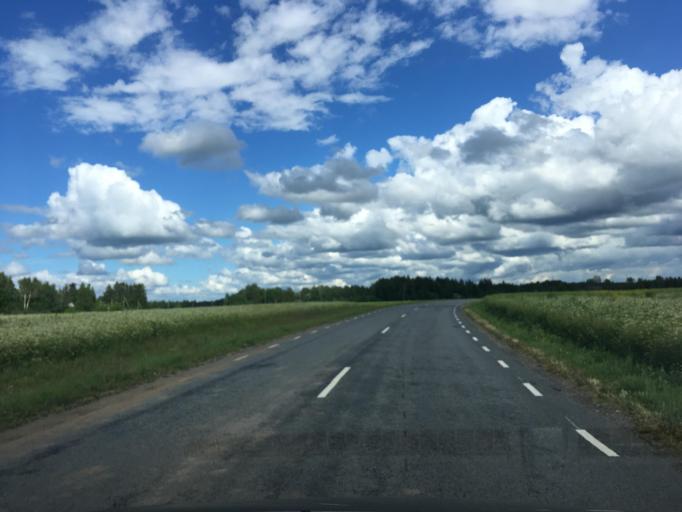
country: EE
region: Paernumaa
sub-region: Halinga vald
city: Parnu-Jaagupi
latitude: 58.6216
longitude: 24.4129
